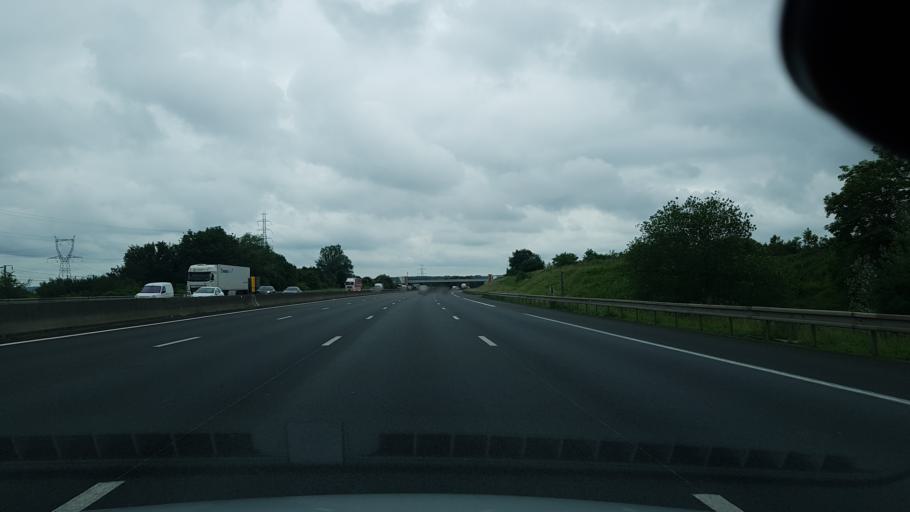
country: FR
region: Ile-de-France
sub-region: Departement de l'Essonne
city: Briis-sous-Forges
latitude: 48.6198
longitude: 2.1311
